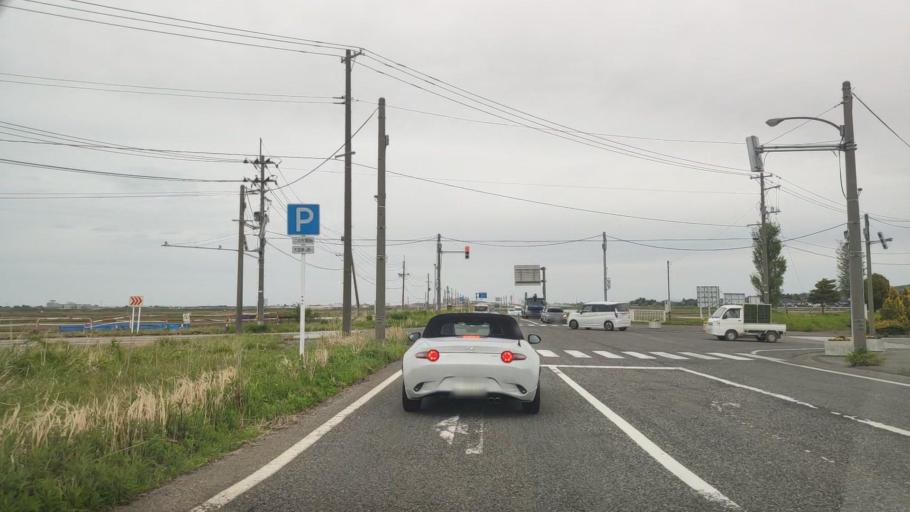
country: JP
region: Niigata
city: Niitsu-honcho
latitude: 37.7708
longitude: 139.1025
